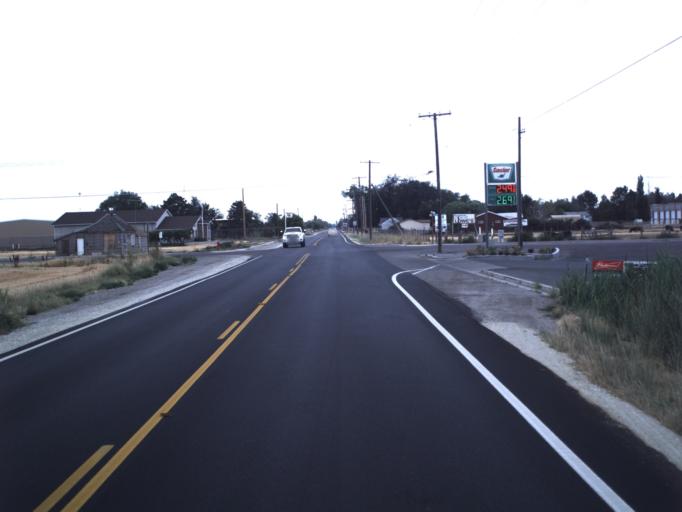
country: US
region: Utah
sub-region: Weber County
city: Hooper
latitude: 41.1639
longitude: -112.1119
